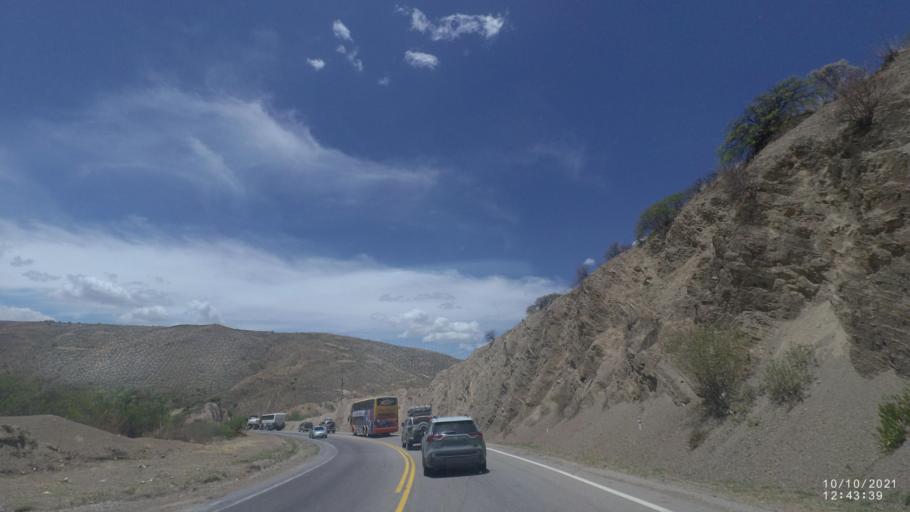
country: BO
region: Cochabamba
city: Irpa Irpa
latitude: -17.6306
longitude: -66.3832
